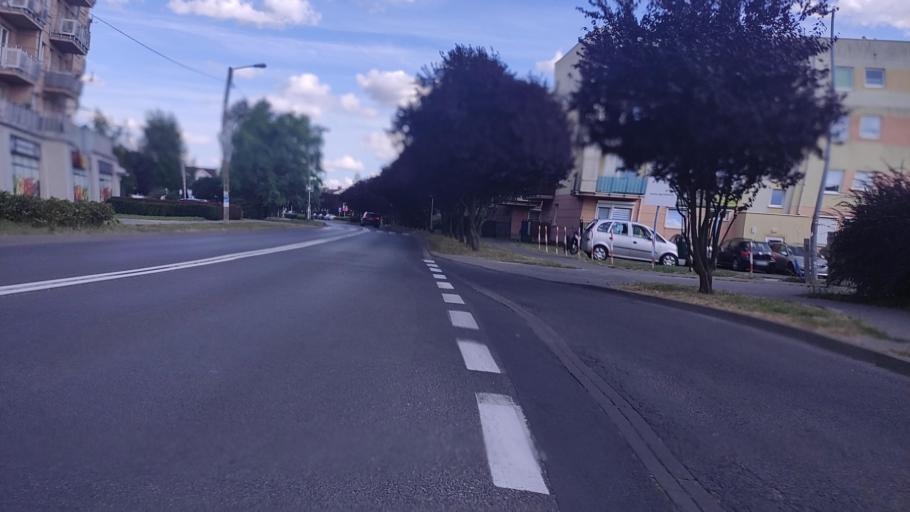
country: PL
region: Greater Poland Voivodeship
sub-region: Powiat poznanski
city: Swarzedz
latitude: 52.3991
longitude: 17.0649
